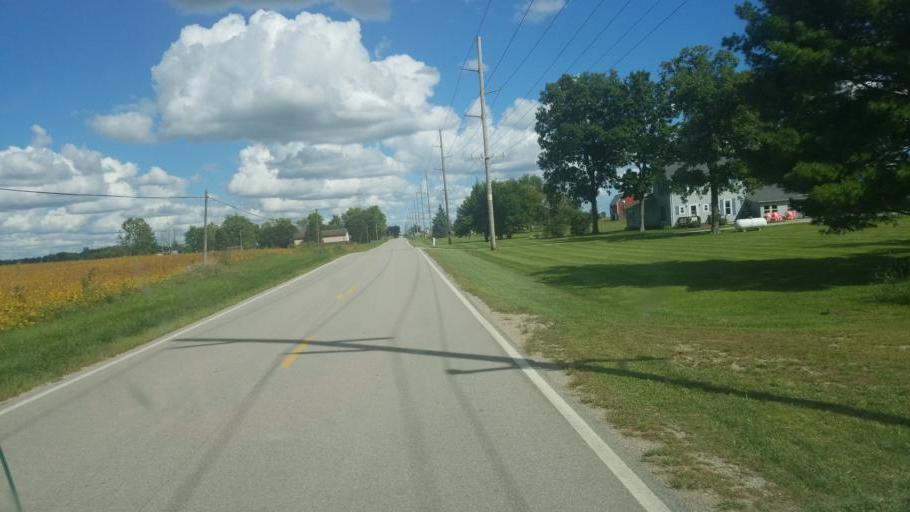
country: US
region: Ohio
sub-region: Union County
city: Richwood
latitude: 40.4393
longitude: -83.4962
